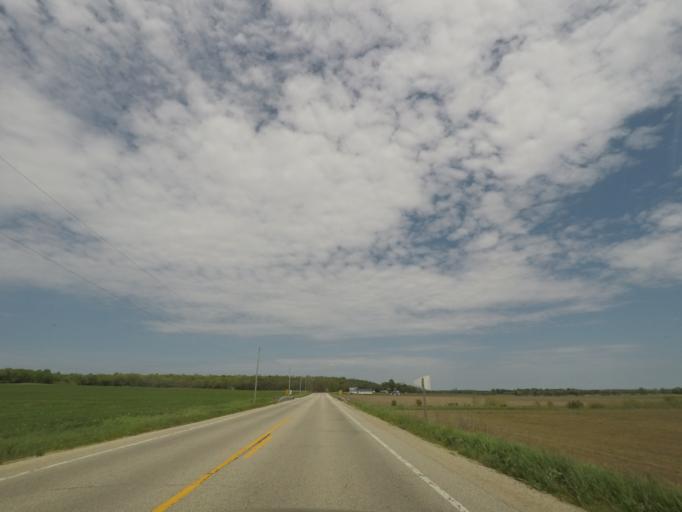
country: US
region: Wisconsin
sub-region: Rock County
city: Evansville
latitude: 42.7197
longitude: -89.2888
